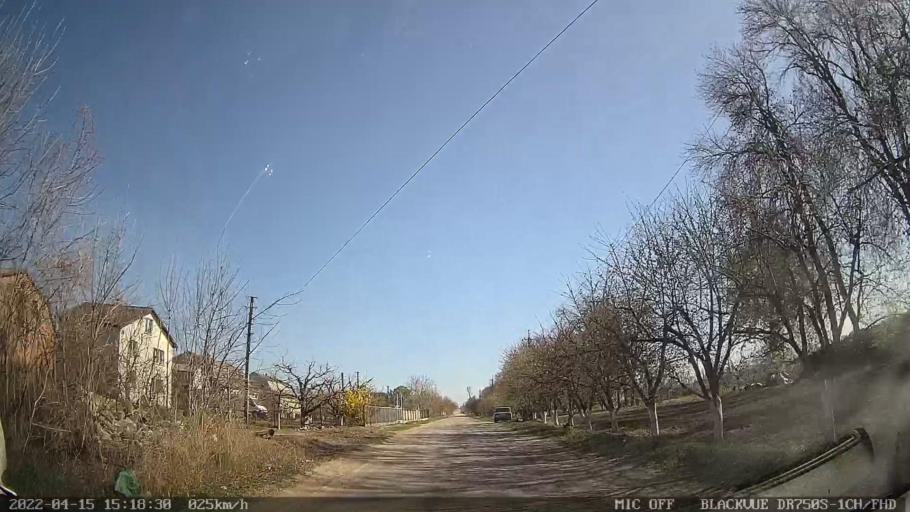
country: MD
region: Raionul Ocnita
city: Otaci
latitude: 48.3905
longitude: 27.9025
